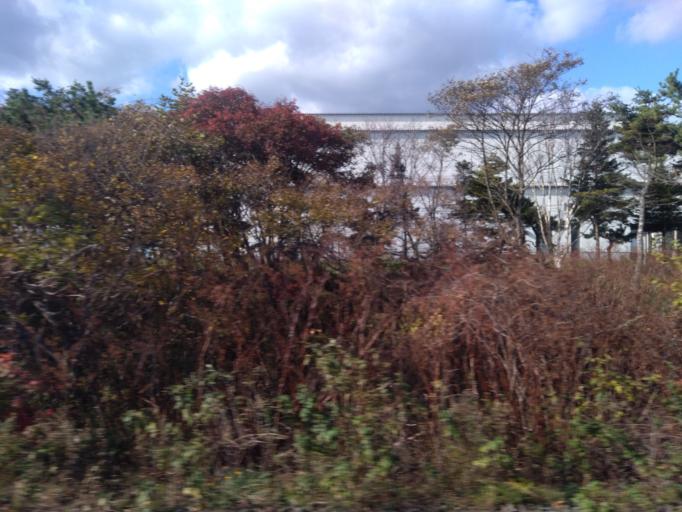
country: JP
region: Hokkaido
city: Shiraoi
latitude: 42.5135
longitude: 141.2934
